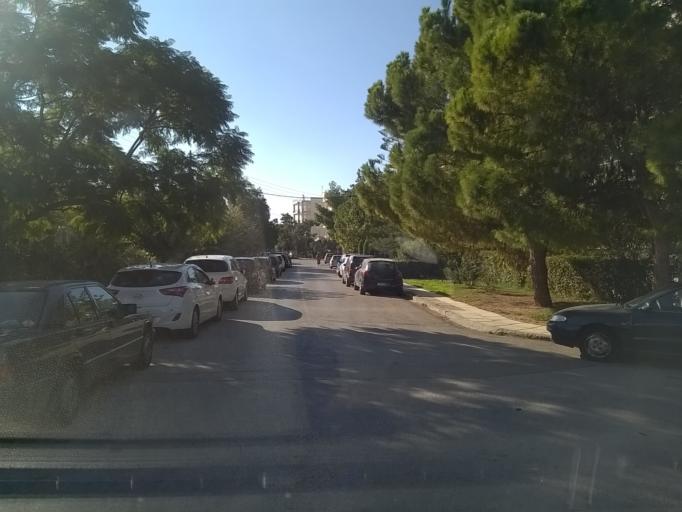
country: GR
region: Attica
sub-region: Nomarchia Athinas
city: Glyfada
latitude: 37.8546
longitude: 23.7597
